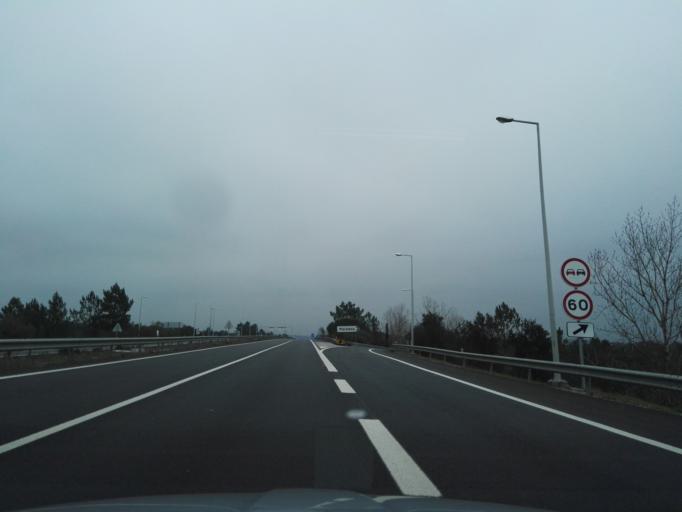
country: PT
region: Setubal
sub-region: Setubal
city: Setubal
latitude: 38.6010
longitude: -8.6763
